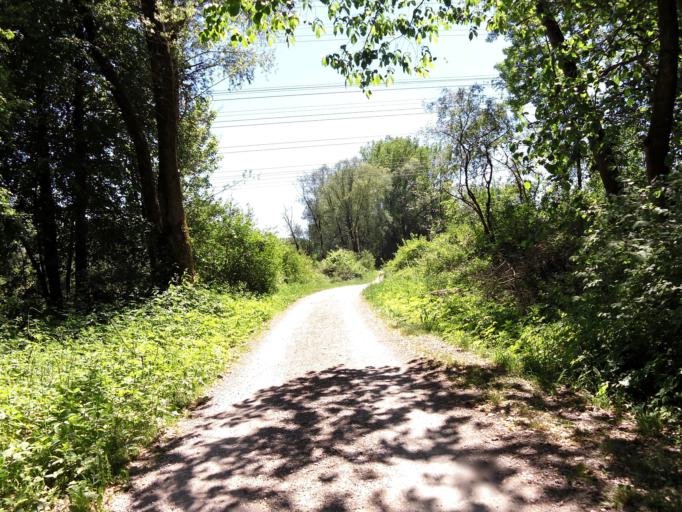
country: DE
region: Bavaria
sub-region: Upper Bavaria
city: Ismaning
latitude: 48.2767
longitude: 11.6914
